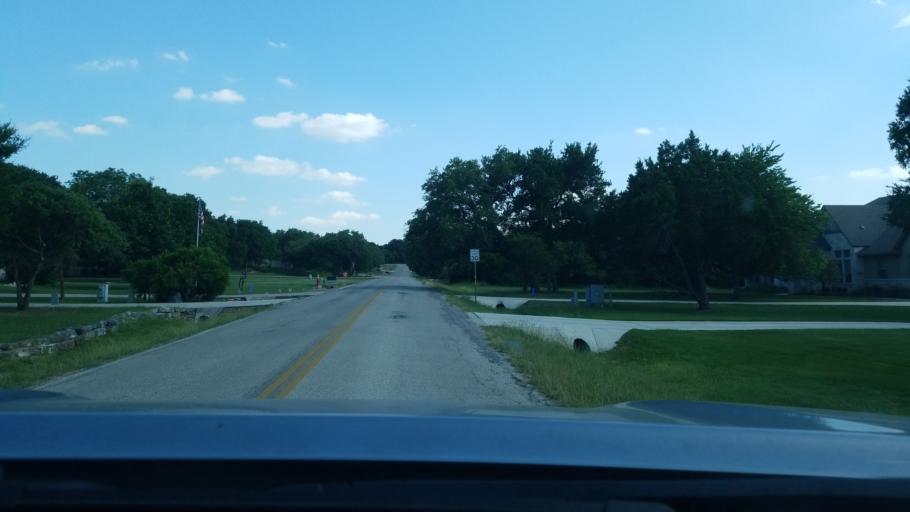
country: US
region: Texas
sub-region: Comal County
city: Bulverde
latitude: 29.8251
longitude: -98.3999
